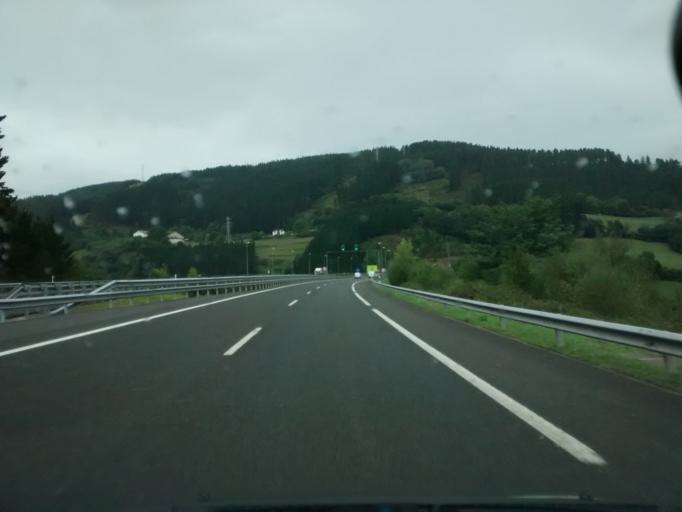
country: ES
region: Basque Country
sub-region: Provincia de Guipuzcoa
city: Bergara
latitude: 43.1017
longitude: -2.4344
